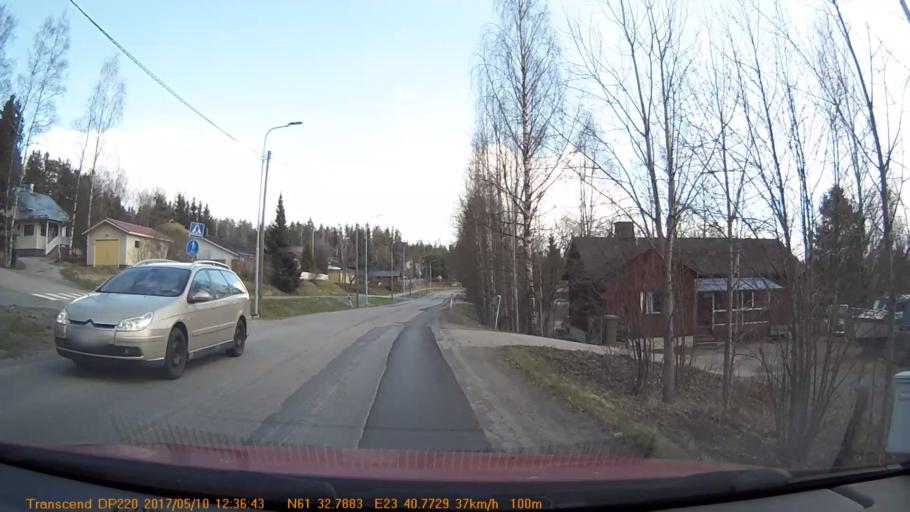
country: FI
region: Pirkanmaa
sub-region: Tampere
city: Yloejaervi
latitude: 61.5465
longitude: 23.6795
